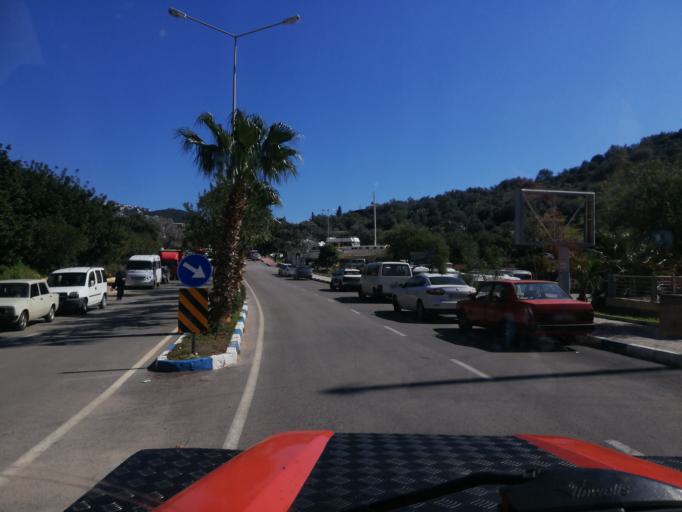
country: TR
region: Antalya
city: Kas
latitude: 36.2032
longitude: 29.6348
